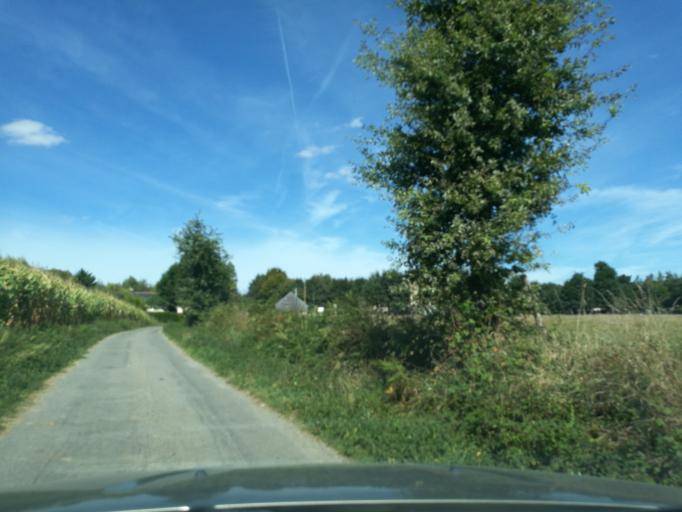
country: FR
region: Brittany
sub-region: Departement d'Ille-et-Vilaine
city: Bedee
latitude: 48.1666
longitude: -1.9487
